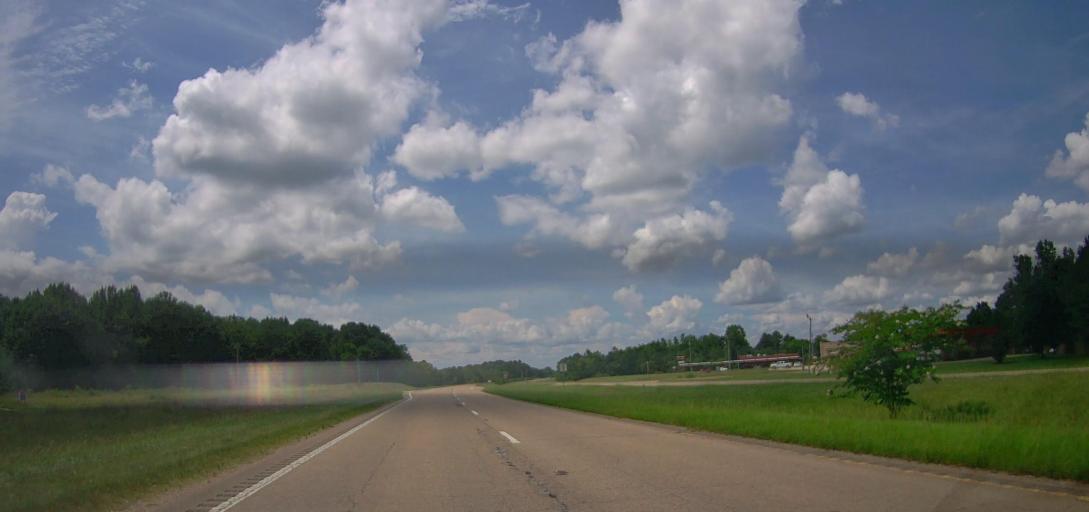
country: US
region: Mississippi
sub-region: Lee County
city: Nettleton
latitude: 34.0758
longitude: -88.6312
